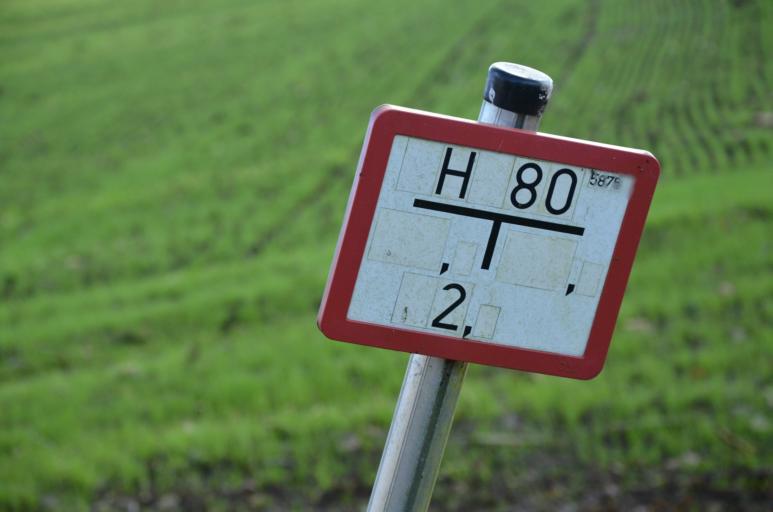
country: BE
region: Flanders
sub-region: Provincie Antwerpen
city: Laakdal
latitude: 51.0955
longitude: 5.0200
